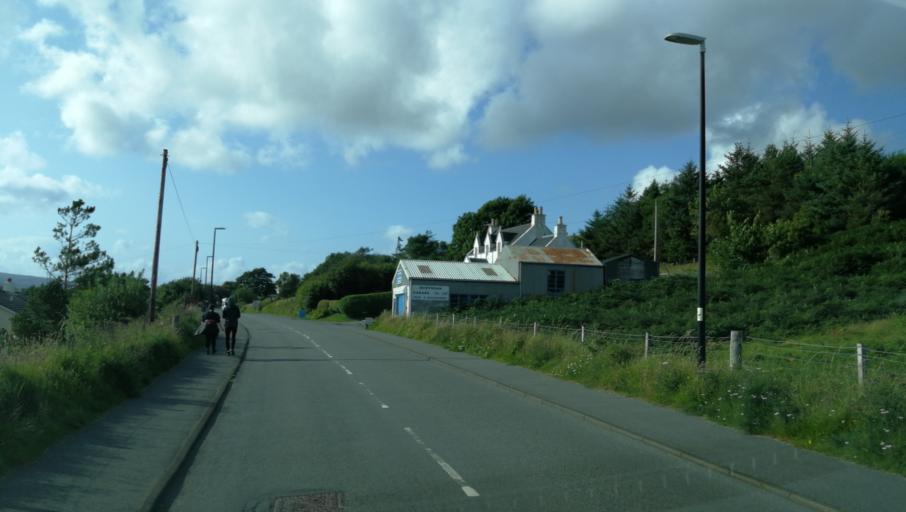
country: GB
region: Scotland
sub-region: Highland
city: Isle of Skye
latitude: 57.4336
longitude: -6.5760
